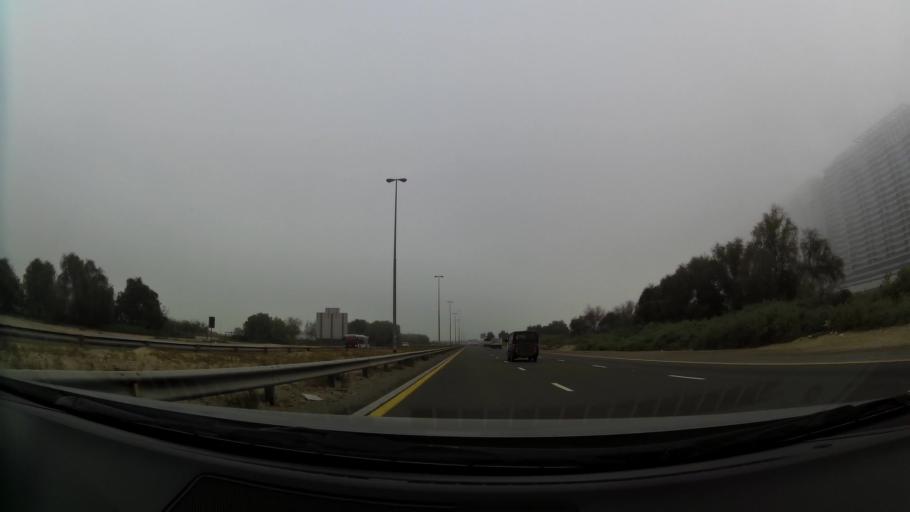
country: AE
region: Dubai
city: Dubai
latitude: 25.0941
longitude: 55.3866
